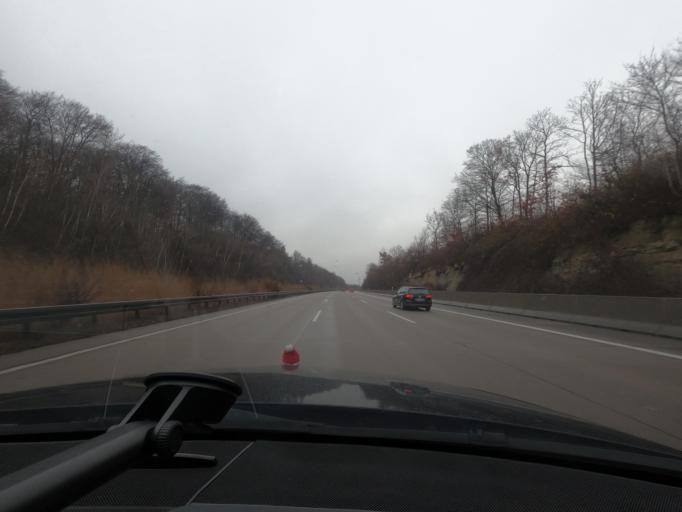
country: DE
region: Lower Saxony
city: Hildesheim
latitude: 52.1371
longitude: 10.0123
